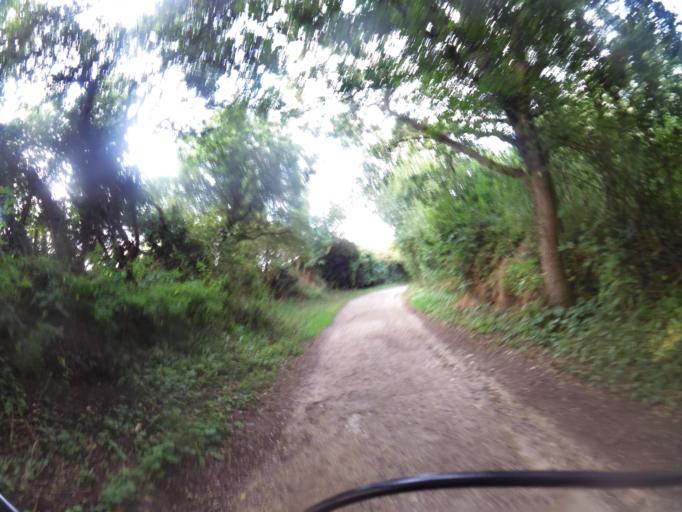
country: GB
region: England
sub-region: Suffolk
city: Ipswich
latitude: 52.0288
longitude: 1.1288
